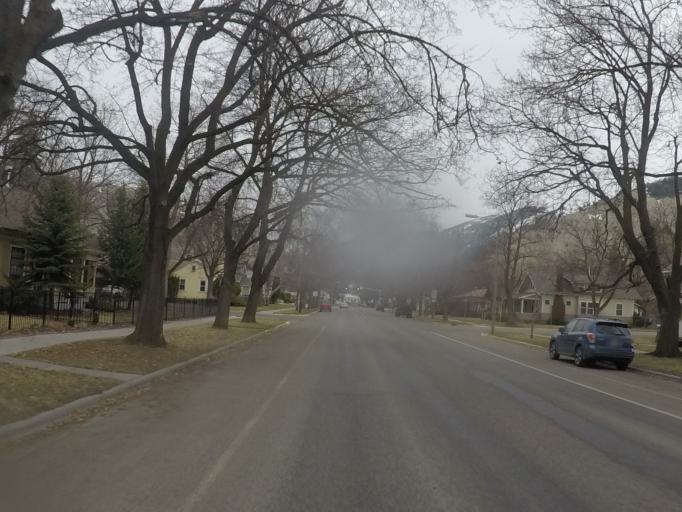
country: US
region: Montana
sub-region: Missoula County
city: Missoula
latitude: 46.8640
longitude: -113.9916
